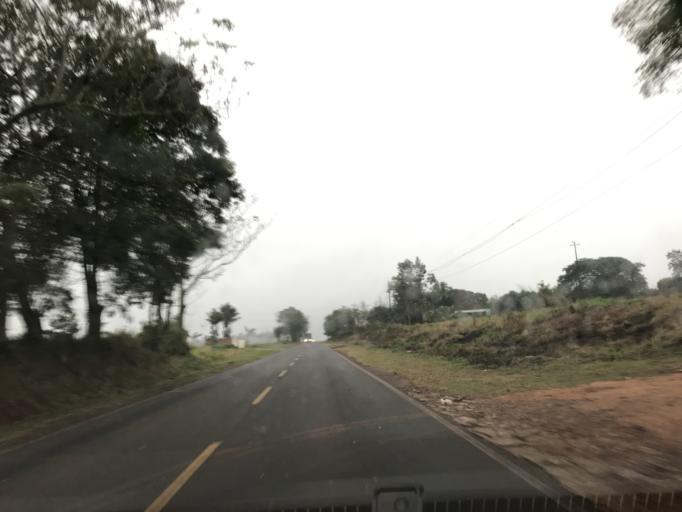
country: PY
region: Canindeyu
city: Salto del Guaira
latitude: -24.1496
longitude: -54.1039
